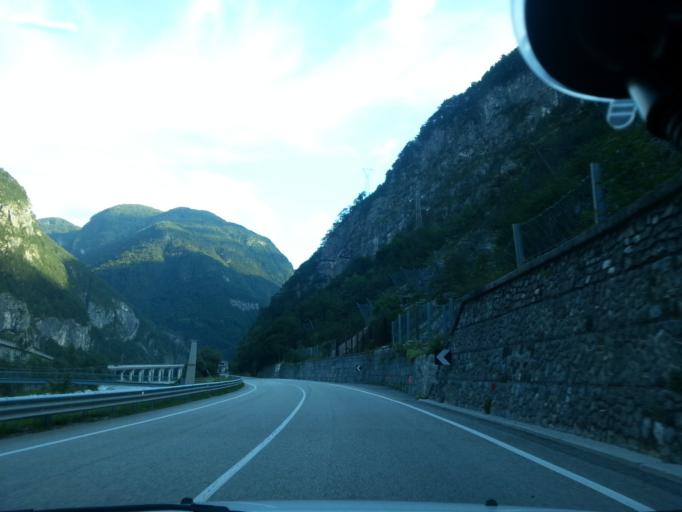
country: IT
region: Friuli Venezia Giulia
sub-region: Provincia di Udine
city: Dogna
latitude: 46.4293
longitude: 13.3150
